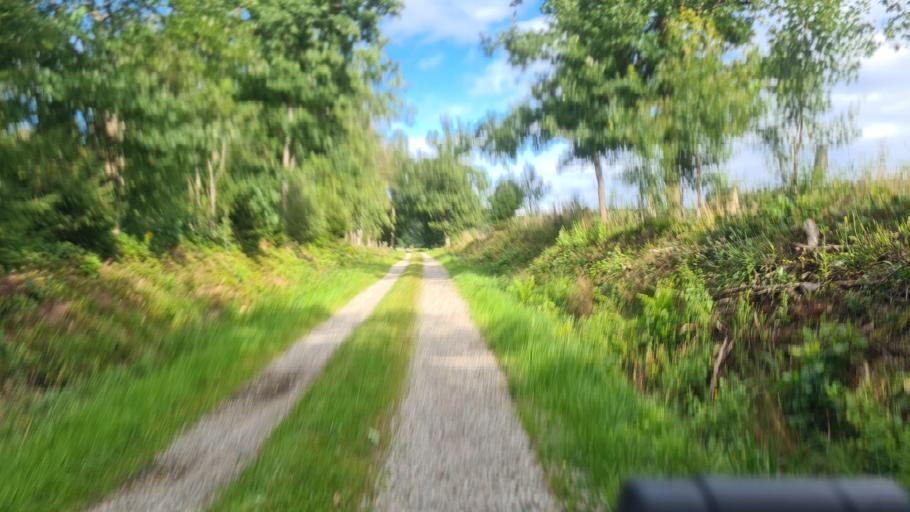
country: SE
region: Kronoberg
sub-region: Ljungby Kommun
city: Ljungby
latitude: 56.8243
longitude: 13.8694
